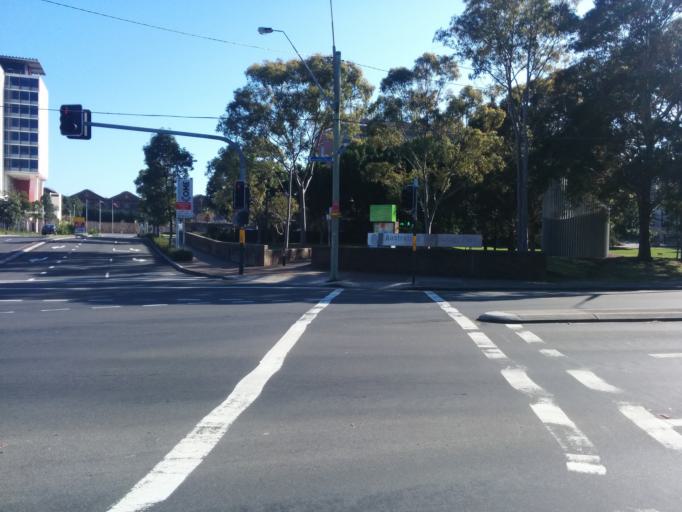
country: AU
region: New South Wales
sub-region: City of Sydney
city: Alexandria
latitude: -33.8976
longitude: 151.1956
